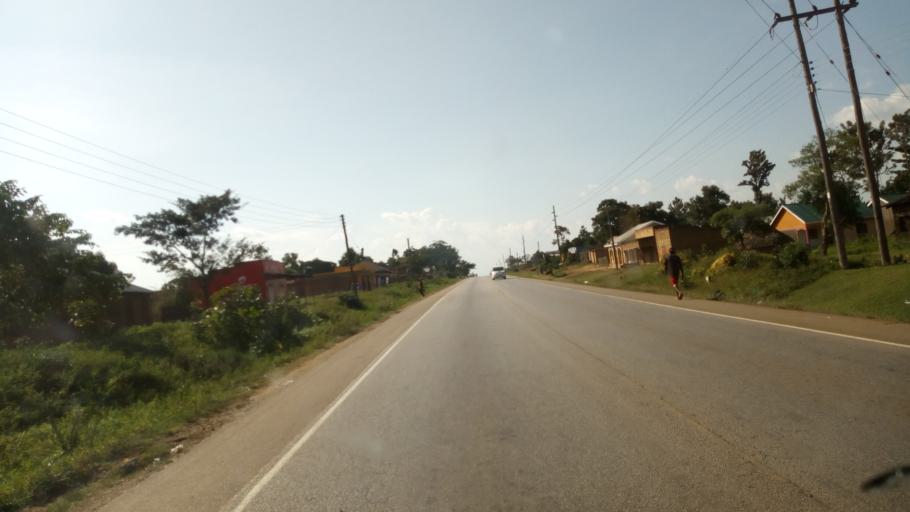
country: UG
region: Eastern Region
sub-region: Bugiri District
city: Bugiri
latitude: 0.5160
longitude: 33.7991
